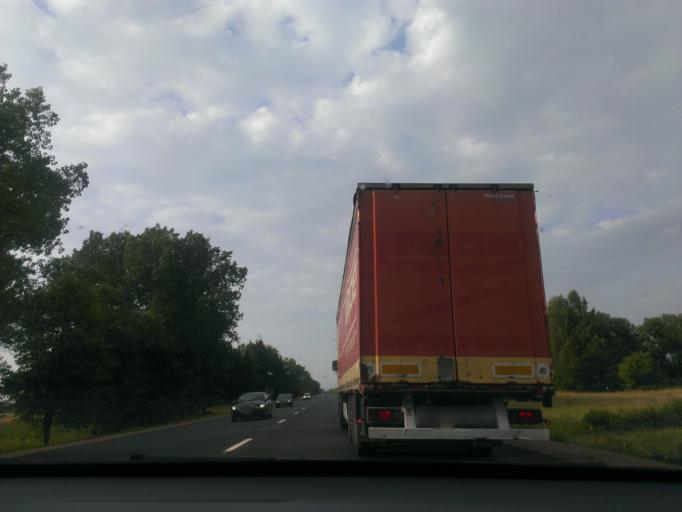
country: LV
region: Lecava
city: Iecava
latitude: 56.6713
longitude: 24.2353
